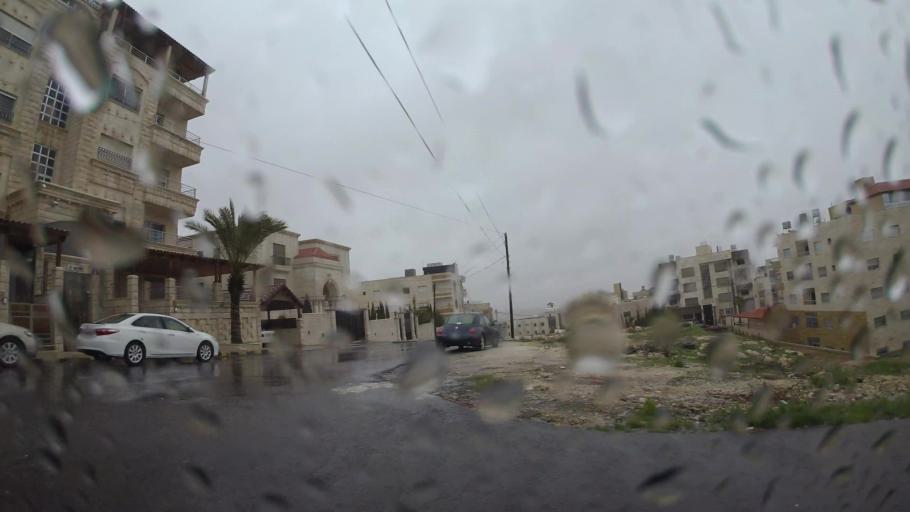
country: JO
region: Amman
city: Al Jubayhah
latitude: 32.0266
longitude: 35.8866
